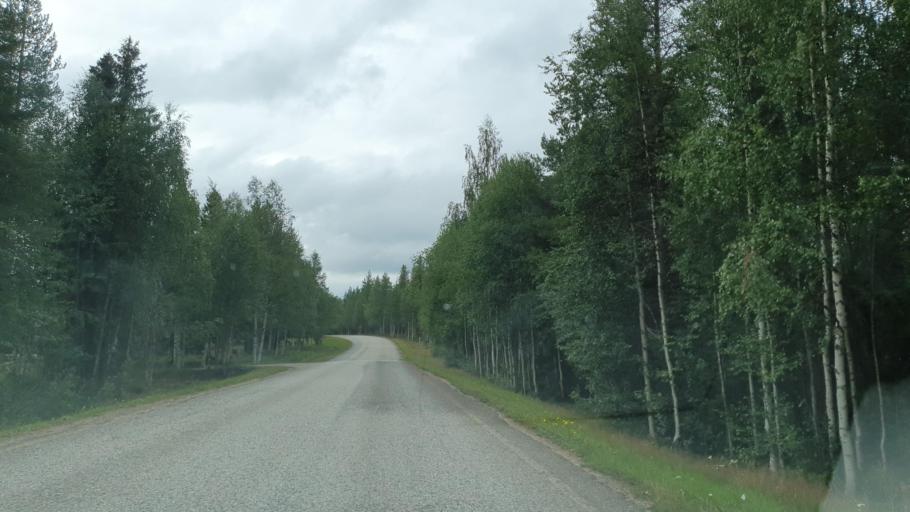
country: FI
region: Lapland
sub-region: Tunturi-Lappi
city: Kolari
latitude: 67.5040
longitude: 24.2633
